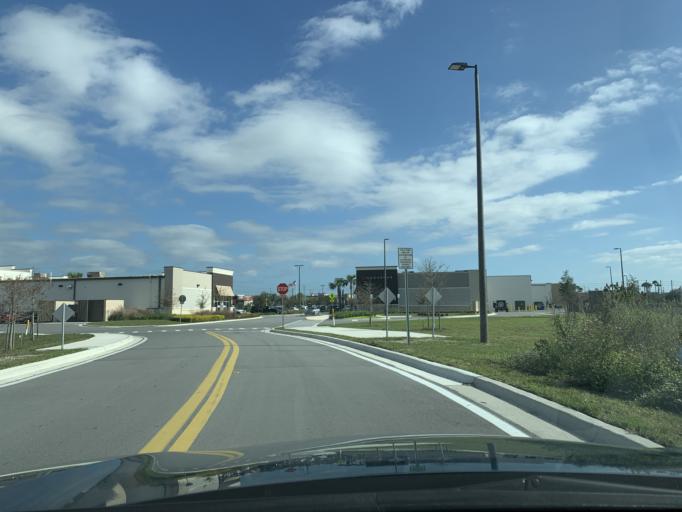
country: US
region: Florida
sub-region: Pasco County
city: Trinity
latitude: 28.2035
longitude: -82.6696
